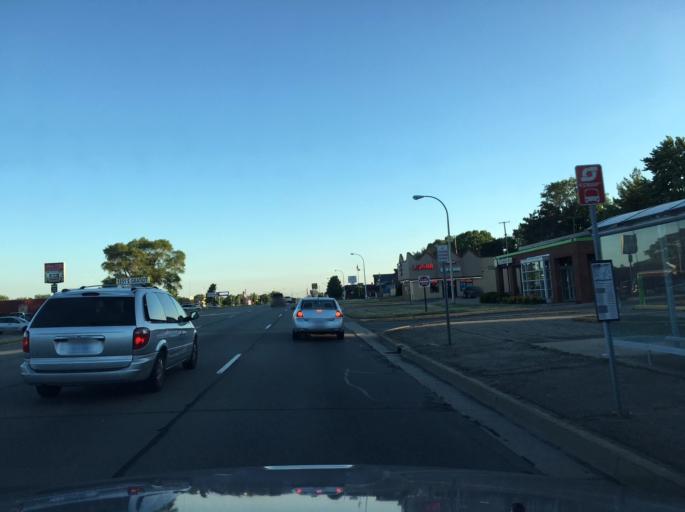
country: US
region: Michigan
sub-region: Macomb County
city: Mount Clemens
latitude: 42.5810
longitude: -82.8858
